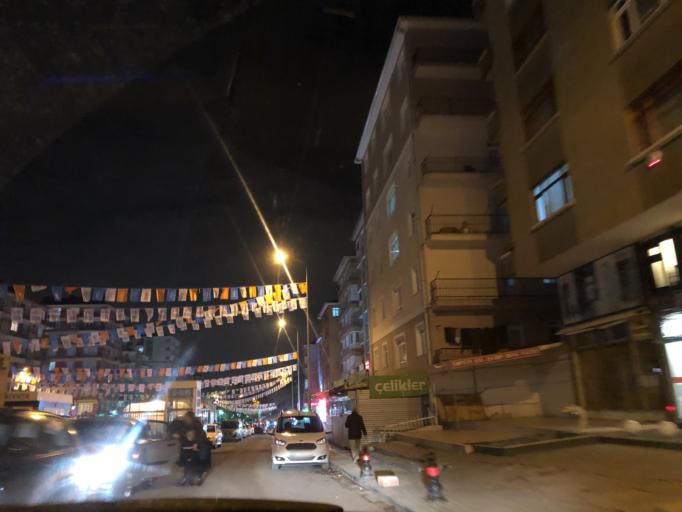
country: TR
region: Ankara
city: Batikent
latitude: 39.9693
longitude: 32.7831
